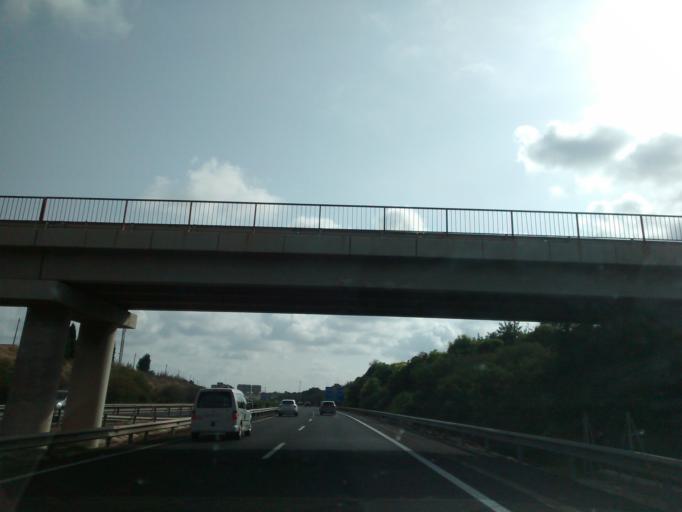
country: ES
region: Valencia
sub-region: Provincia de Alicante
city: el Campello
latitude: 38.4324
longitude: -0.4119
